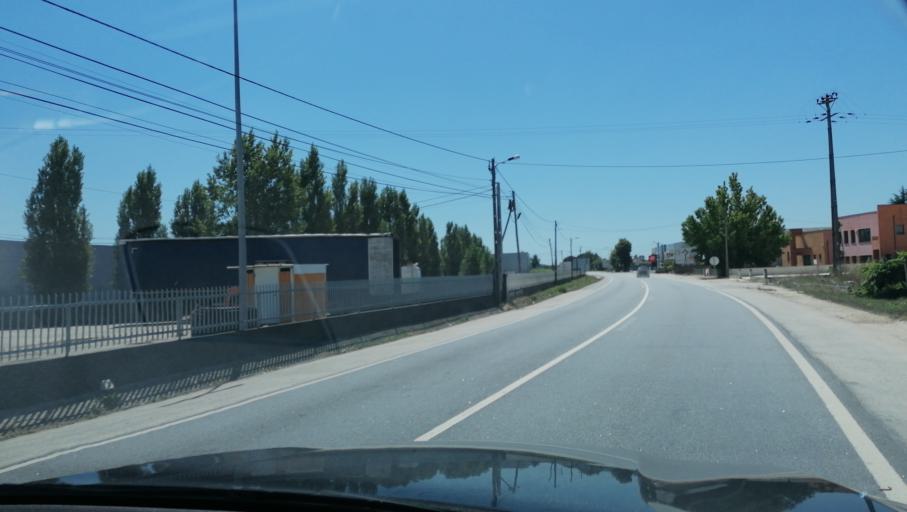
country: PT
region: Aveiro
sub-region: Anadia
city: Arcos
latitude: 40.4646
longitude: -8.4562
